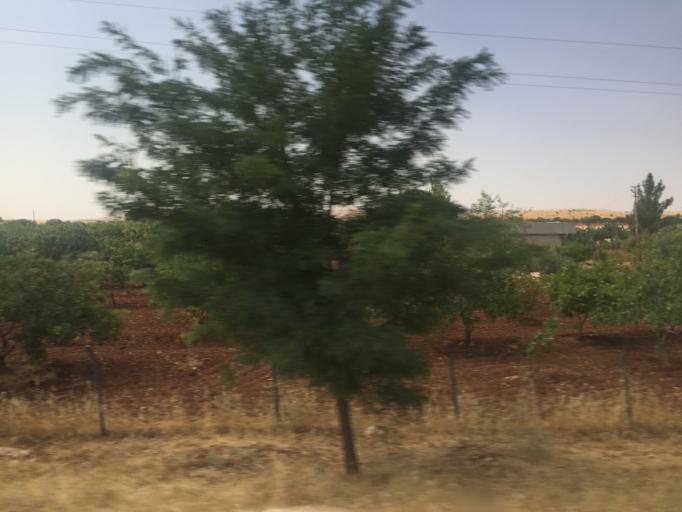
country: TR
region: Sanliurfa
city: Akziyaret
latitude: 37.3898
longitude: 38.8592
